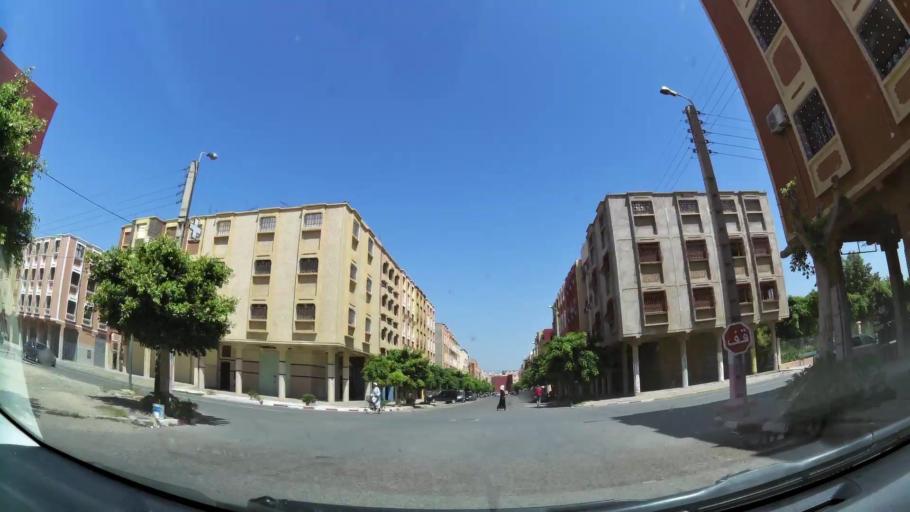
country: MA
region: Souss-Massa-Draa
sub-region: Inezgane-Ait Mellou
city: Inezgane
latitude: 30.3355
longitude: -9.5019
